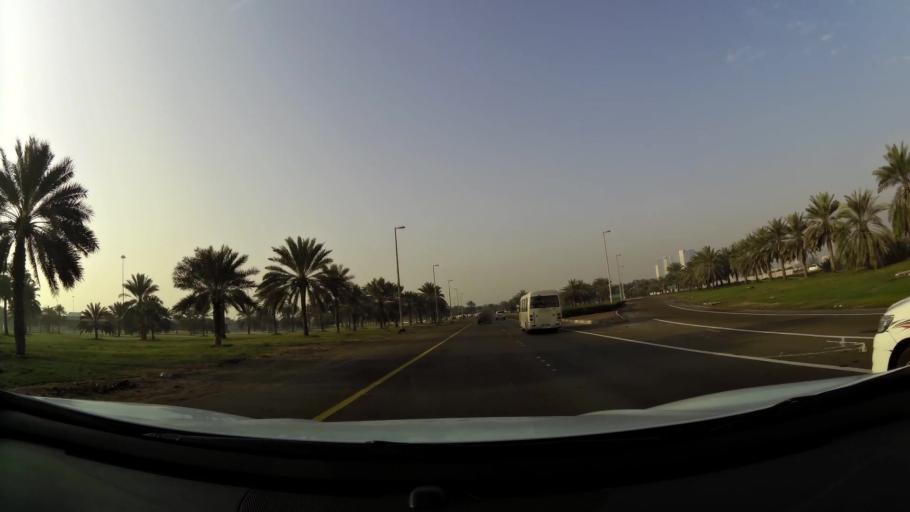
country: AE
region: Abu Dhabi
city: Abu Dhabi
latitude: 24.4225
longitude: 54.4751
